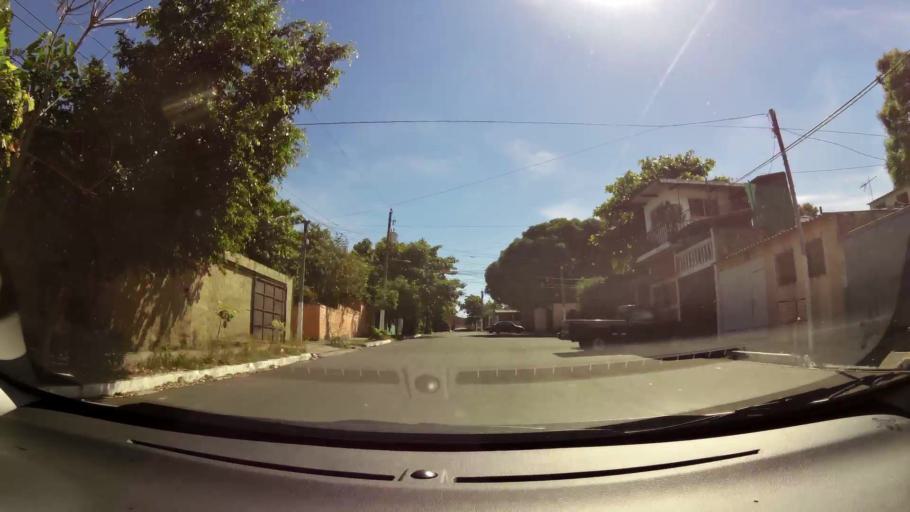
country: SV
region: San Salvador
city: Apopa
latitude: 13.8090
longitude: -89.1780
